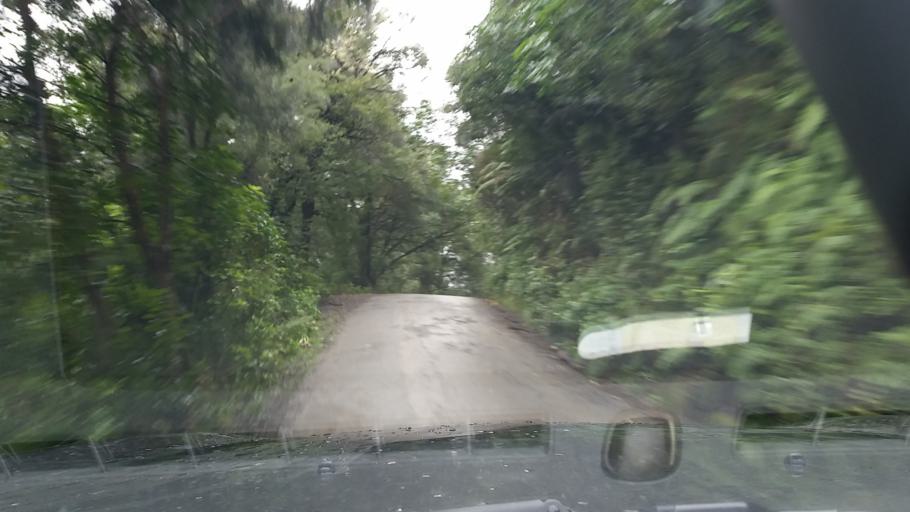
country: NZ
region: Marlborough
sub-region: Marlborough District
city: Picton
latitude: -41.2872
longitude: 174.0375
